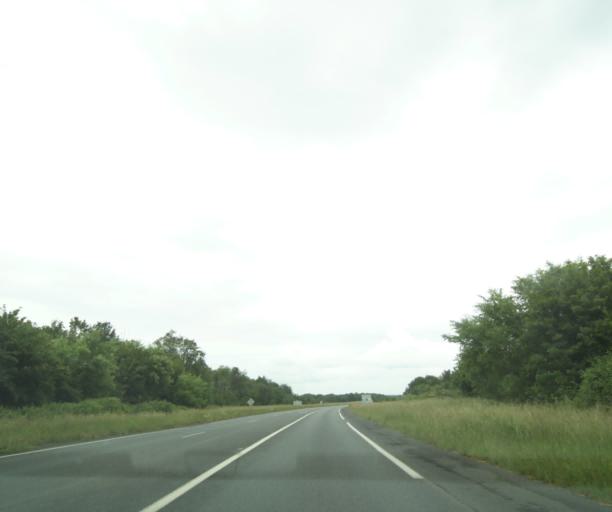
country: FR
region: Poitou-Charentes
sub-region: Departement des Deux-Sevres
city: Saint-Varent
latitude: 46.8623
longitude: -0.2085
